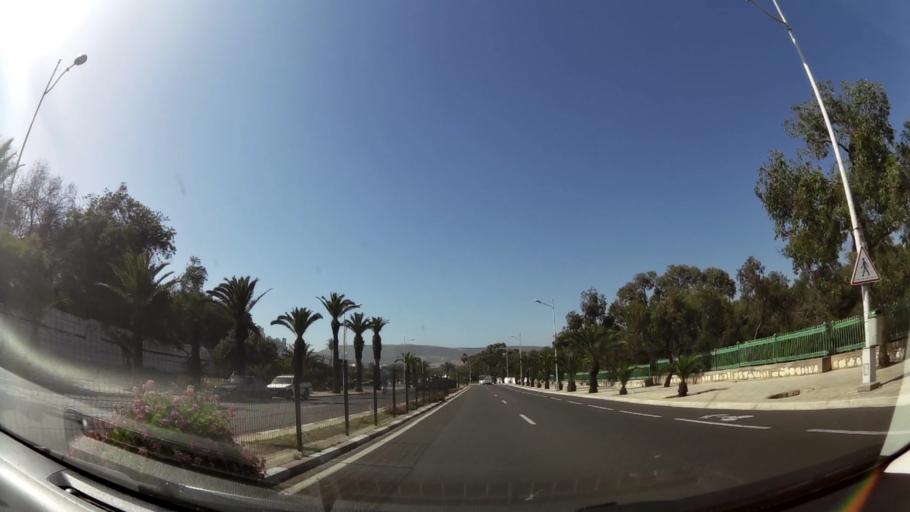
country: MA
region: Souss-Massa-Draa
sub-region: Agadir-Ida-ou-Tnan
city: Agadir
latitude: 30.4164
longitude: -9.5993
